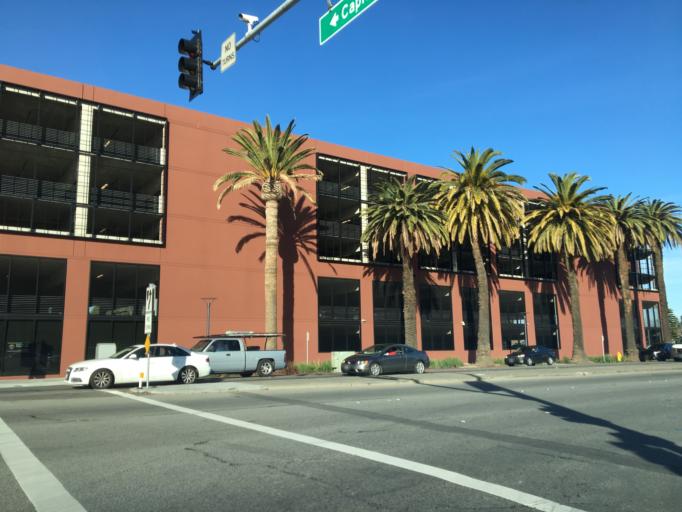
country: US
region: California
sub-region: San Mateo County
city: East Palo Alto
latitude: 37.4625
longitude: -122.1405
